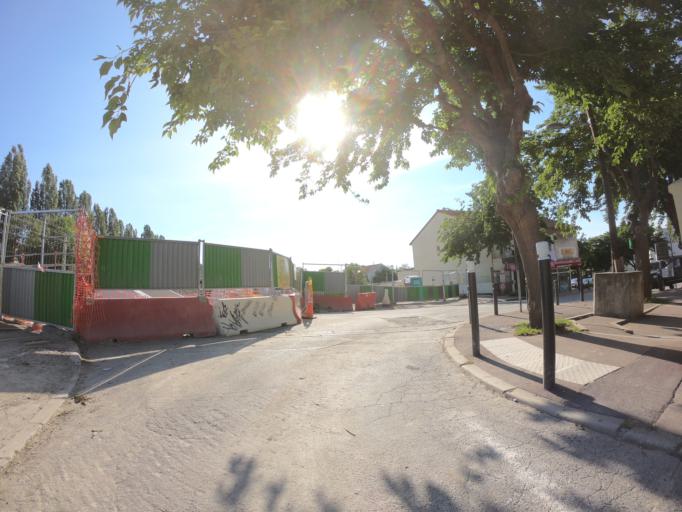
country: FR
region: Ile-de-France
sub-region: Departement des Hauts-de-Seine
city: Antony
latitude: 48.7426
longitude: 2.2973
